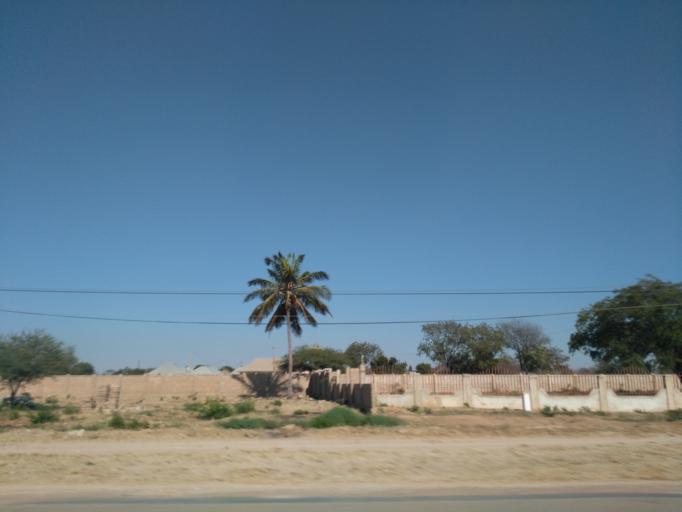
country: TZ
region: Dodoma
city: Dodoma
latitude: -6.1197
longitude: 35.7467
